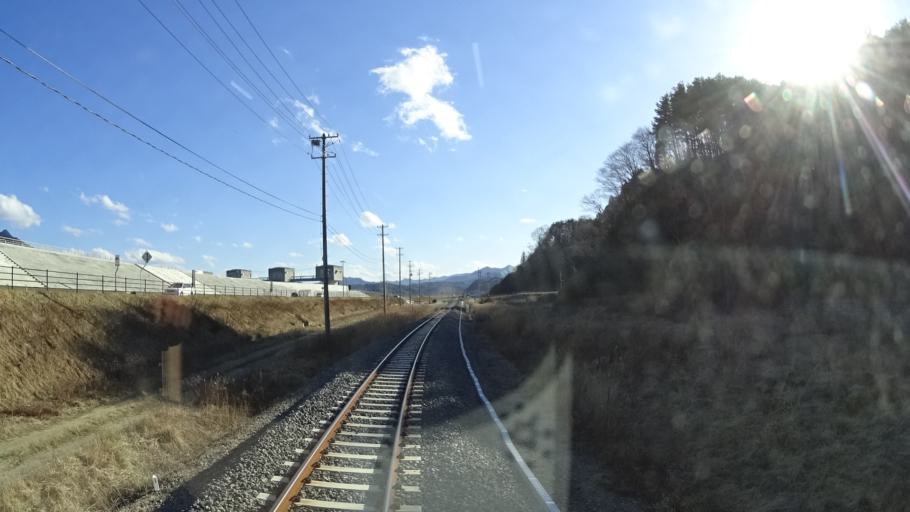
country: JP
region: Iwate
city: Miyako
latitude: 39.5878
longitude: 141.9456
